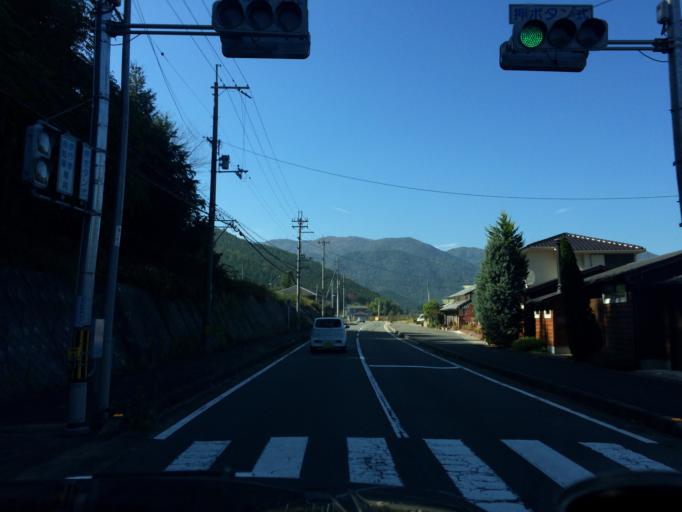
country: JP
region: Kyoto
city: Kameoka
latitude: 35.0484
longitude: 135.4930
